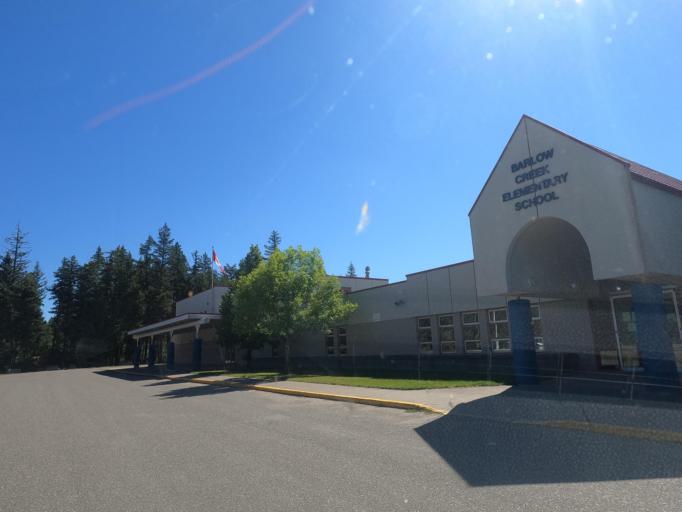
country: CA
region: British Columbia
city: Quesnel
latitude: 53.0206
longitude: -122.4551
